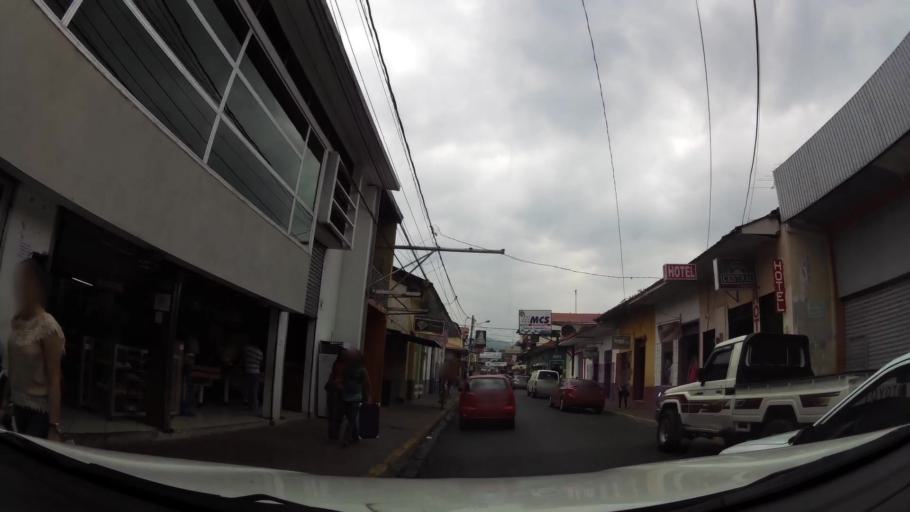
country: NI
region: Matagalpa
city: Matagalpa
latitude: 12.9243
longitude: -85.9195
